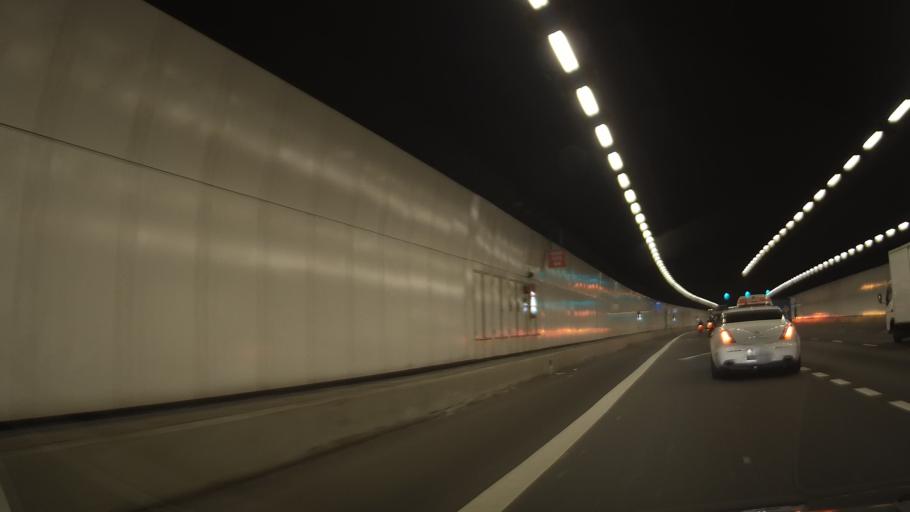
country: SG
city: Singapore
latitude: 1.3320
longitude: 103.8903
